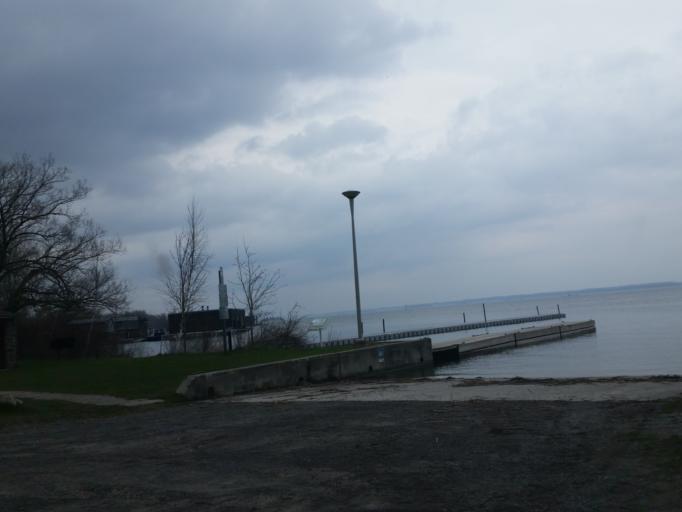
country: US
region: New York
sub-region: Jefferson County
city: Alexandria Bay
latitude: 44.4524
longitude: -75.8600
